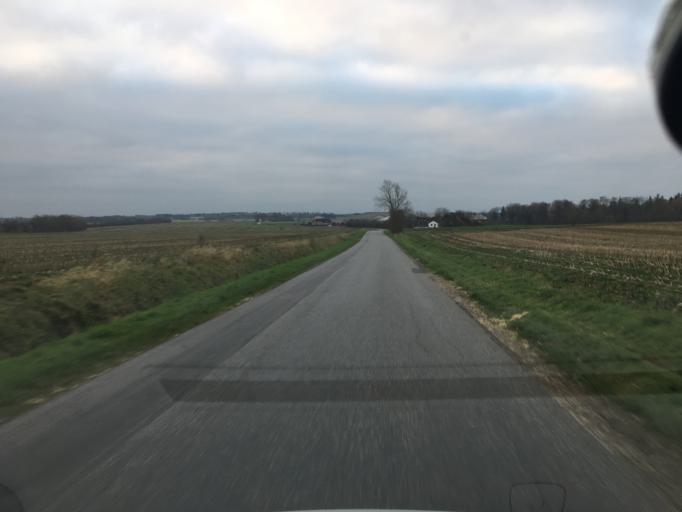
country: DK
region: South Denmark
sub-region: Tonder Kommune
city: Logumkloster
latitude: 55.0702
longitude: 9.0683
